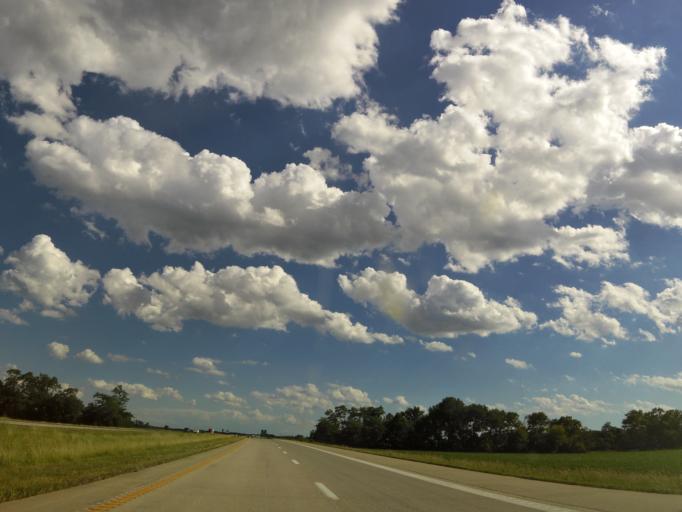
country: US
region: Missouri
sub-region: Clark County
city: Kahoka
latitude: 40.4184
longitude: -91.5729
